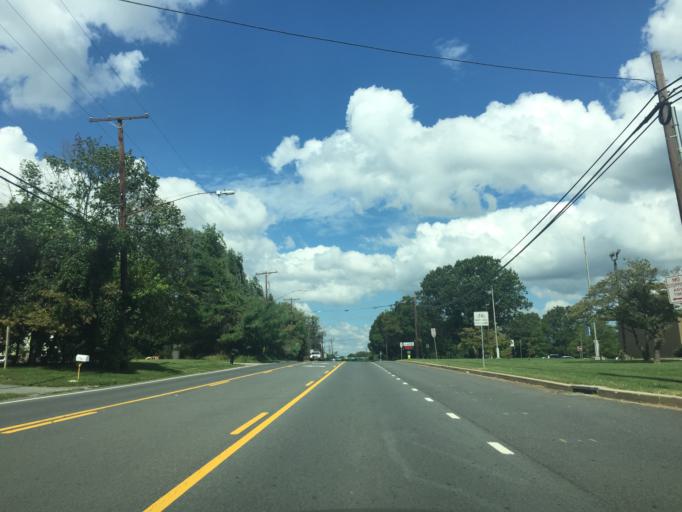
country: US
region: Maryland
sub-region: Montgomery County
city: Redland
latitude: 39.1303
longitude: -77.1192
